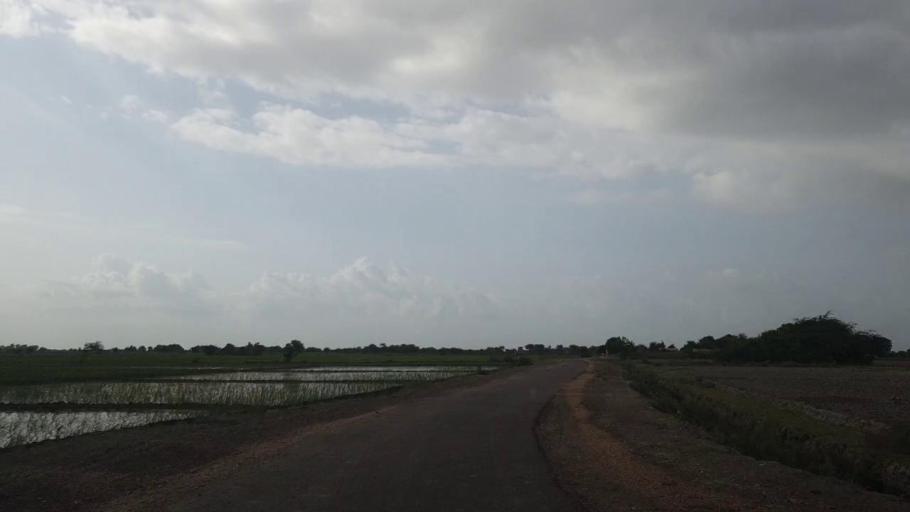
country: PK
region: Sindh
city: Kadhan
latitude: 24.5988
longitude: 69.0566
